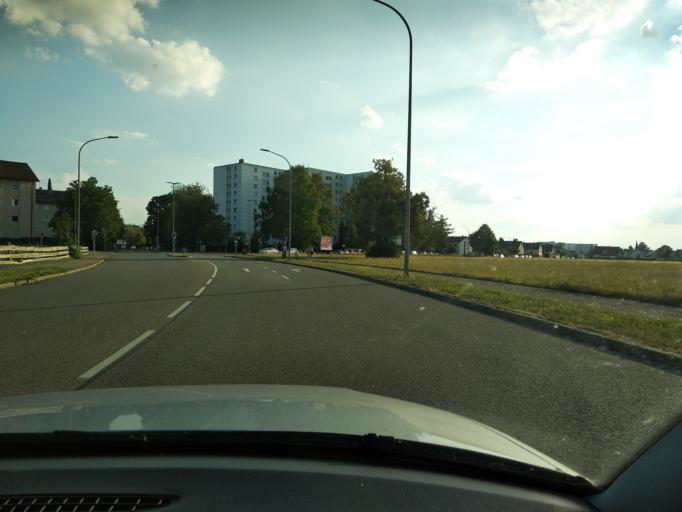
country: DE
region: Bavaria
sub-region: Swabia
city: Memmingen
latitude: 47.9942
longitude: 10.1766
